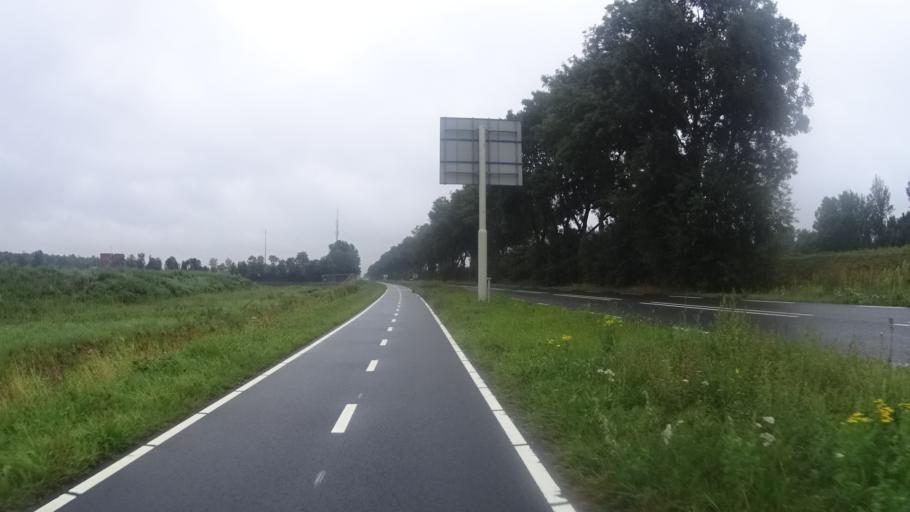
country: NL
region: Groningen
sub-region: Gemeente  Oldambt
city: Winschoten
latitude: 53.1639
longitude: 7.0028
